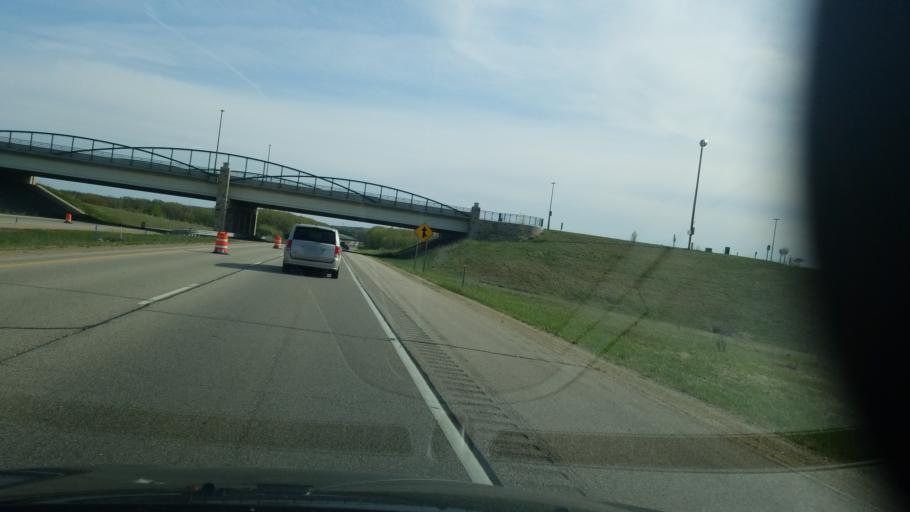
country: US
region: Wisconsin
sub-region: Dane County
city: Madison
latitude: 43.0106
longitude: -89.3825
